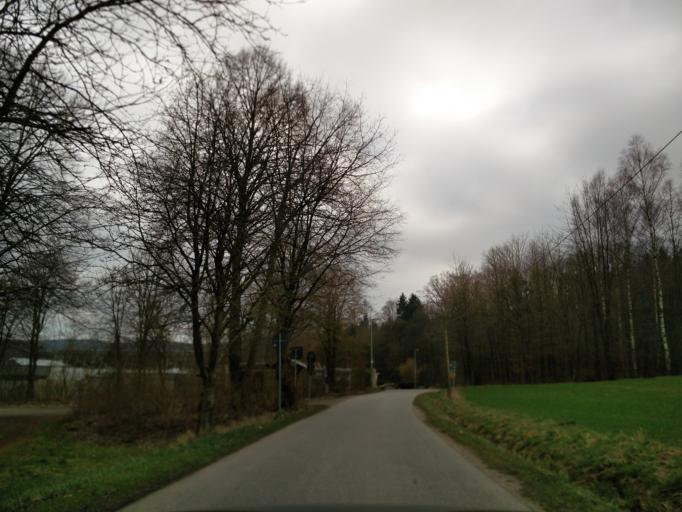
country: DE
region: North Rhine-Westphalia
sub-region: Regierungsbezirk Detmold
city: Willebadessen
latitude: 51.5222
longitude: 9.0044
